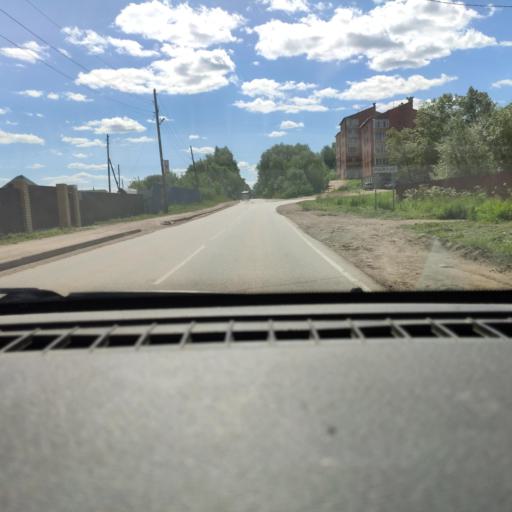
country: RU
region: Perm
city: Chaykovskaya
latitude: 58.1071
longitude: 55.5785
